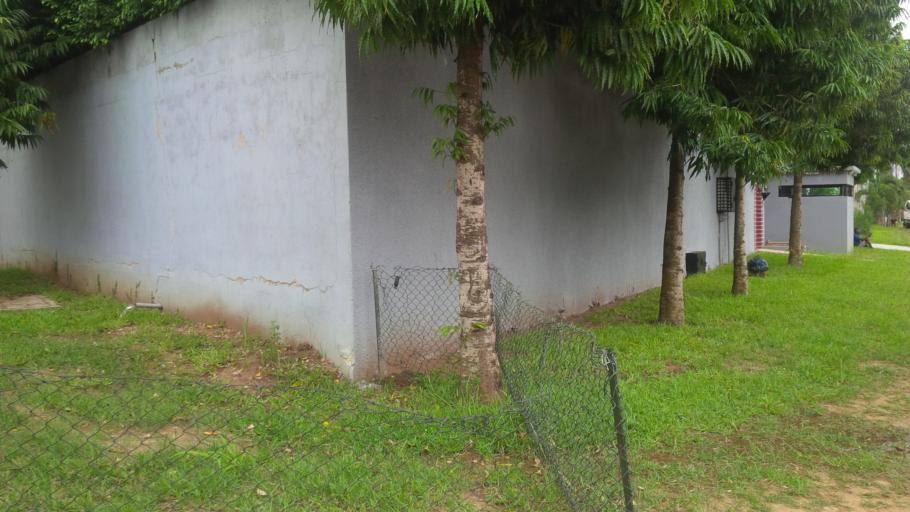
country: CI
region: Lagunes
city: Abidjan
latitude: 5.3447
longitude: -4.0056
